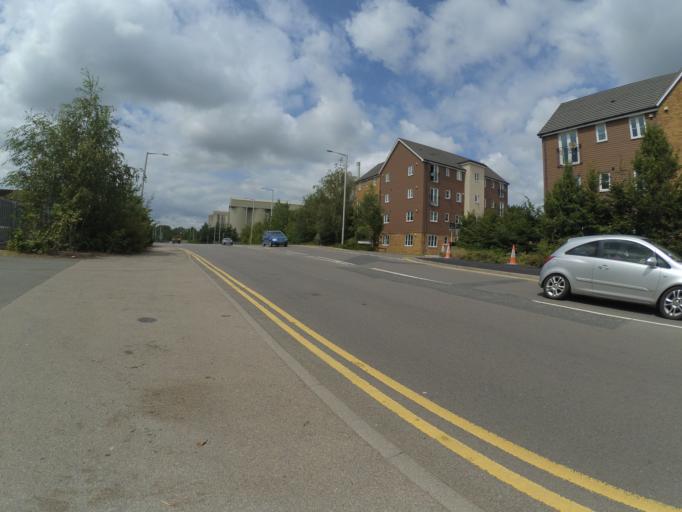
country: GB
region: England
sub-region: Warwickshire
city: Rugby
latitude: 52.3752
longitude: -1.2810
